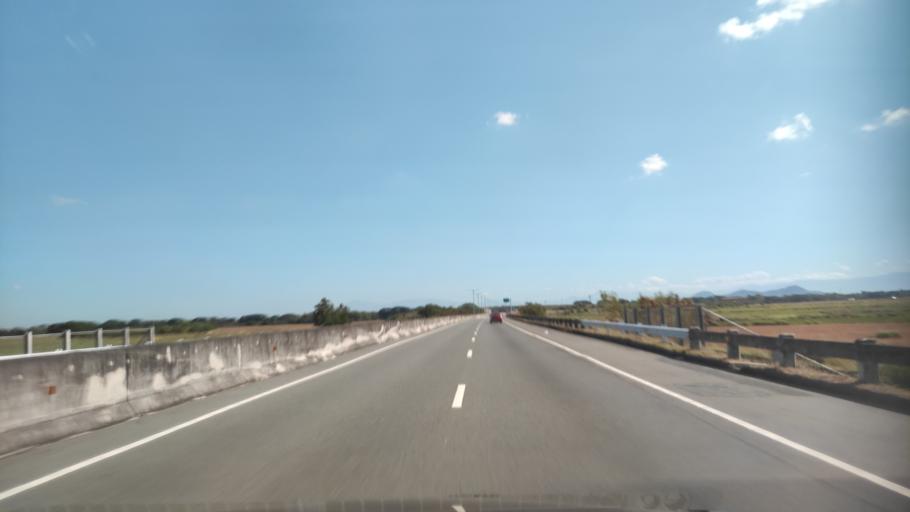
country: PH
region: Central Luzon
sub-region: Province of Tarlac
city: Estacion
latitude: 15.7094
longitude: 120.6120
